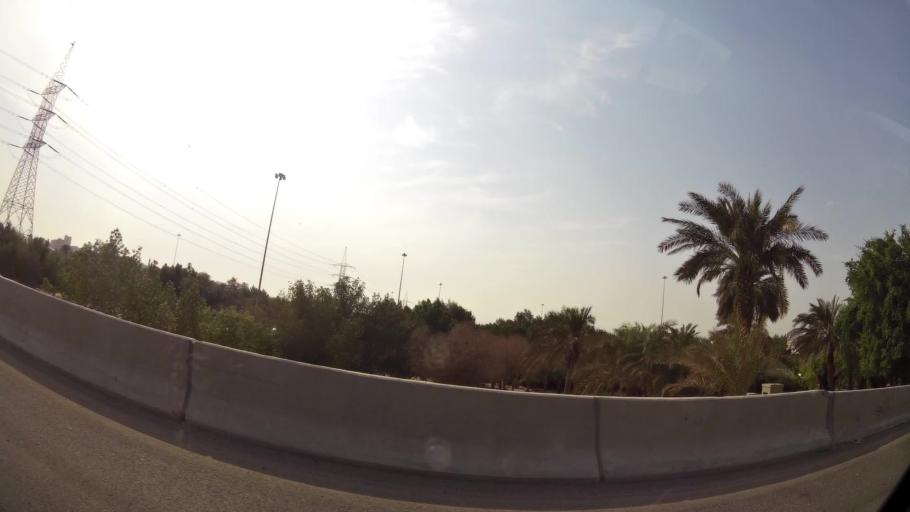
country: KW
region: Al Farwaniyah
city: Al Farwaniyah
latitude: 29.3044
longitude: 47.9788
